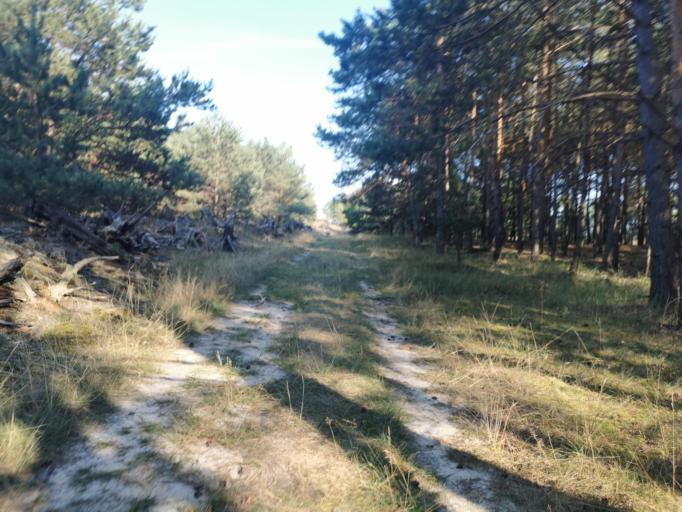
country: SK
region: Trnavsky
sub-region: Okres Senica
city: Senica
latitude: 48.6433
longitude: 17.2935
